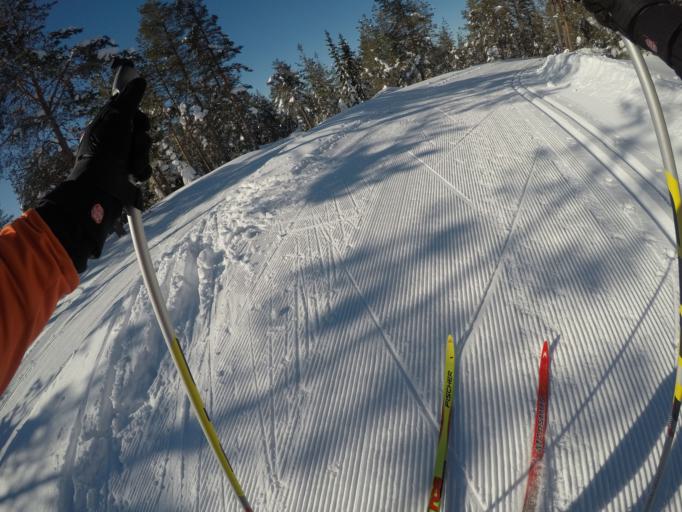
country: SE
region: Vaesternorrland
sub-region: Sundsvalls Kommun
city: Sundsvall
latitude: 62.3662
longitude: 17.3043
